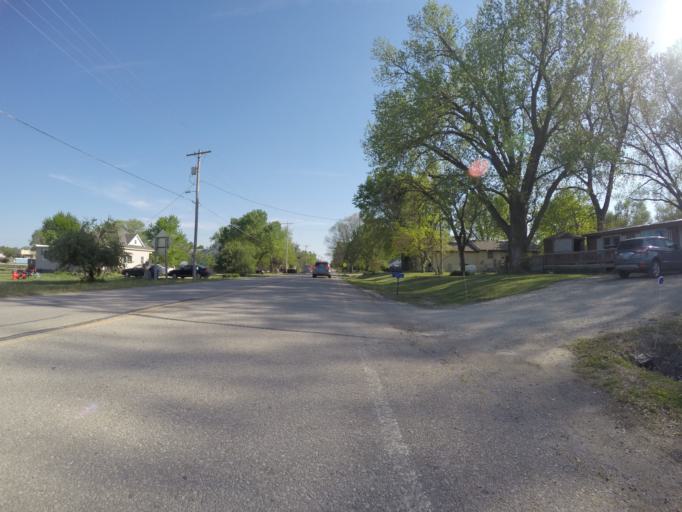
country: US
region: Kansas
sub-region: Riley County
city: Fort Riley North
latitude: 39.3019
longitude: -96.8309
